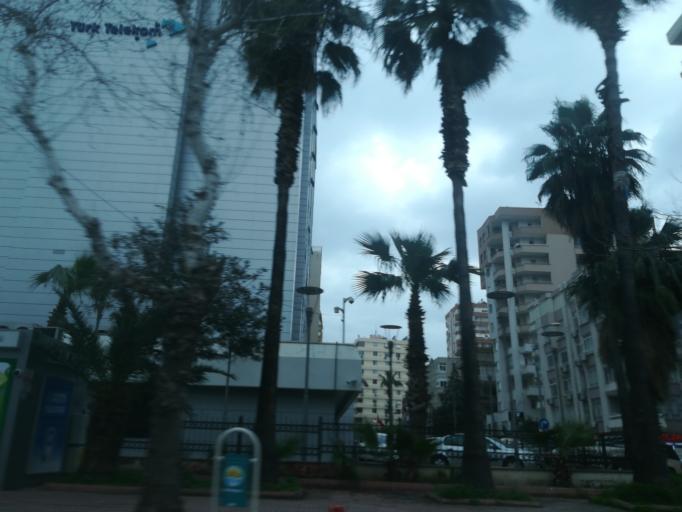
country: TR
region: Adana
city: Adana
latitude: 37.0023
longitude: 35.3198
